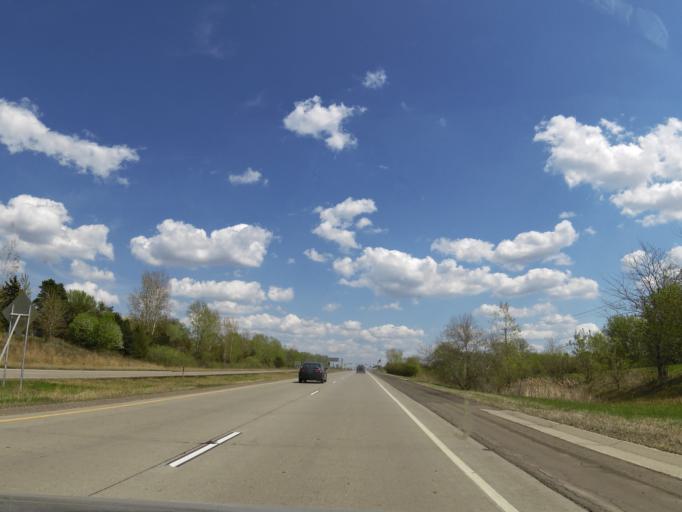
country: US
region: Minnesota
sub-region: Dakota County
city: Mendota Heights
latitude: 44.8836
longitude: -93.1545
